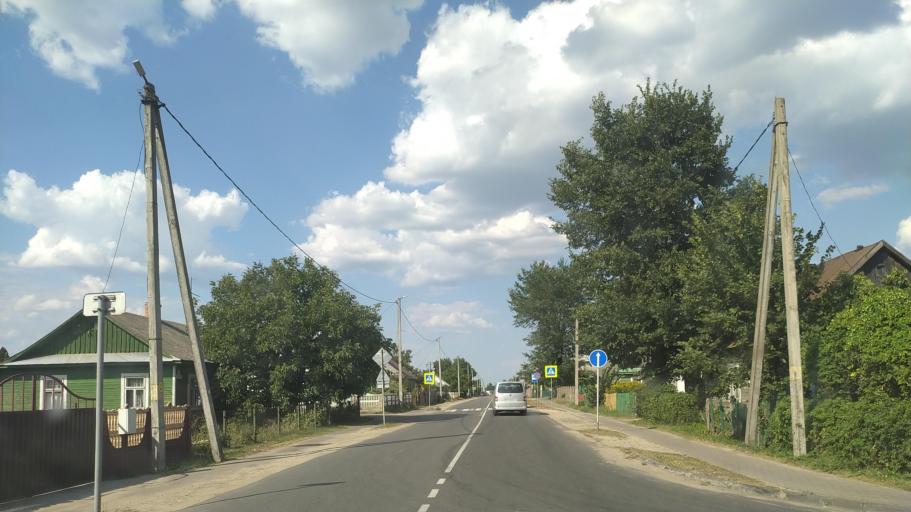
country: BY
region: Brest
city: Drahichyn
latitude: 52.1929
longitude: 25.1472
